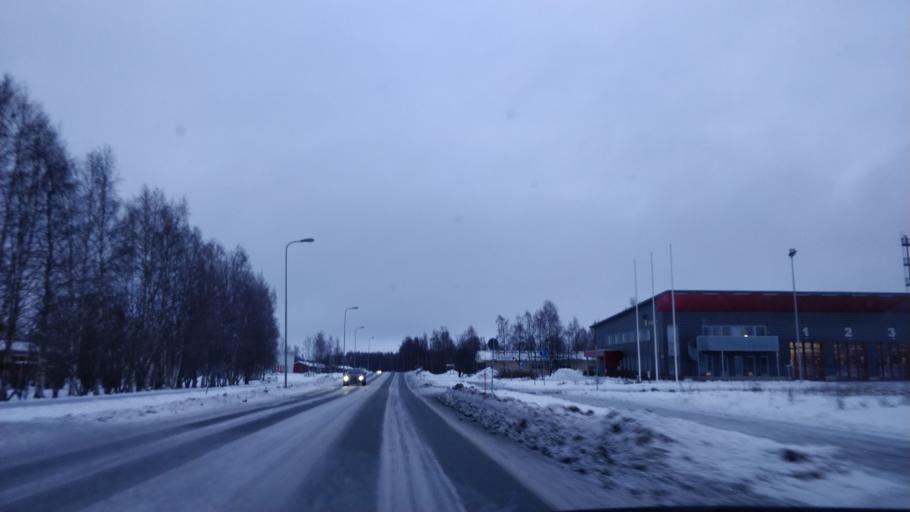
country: FI
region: Lapland
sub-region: Kemi-Tornio
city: Kemi
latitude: 65.7434
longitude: 24.5897
